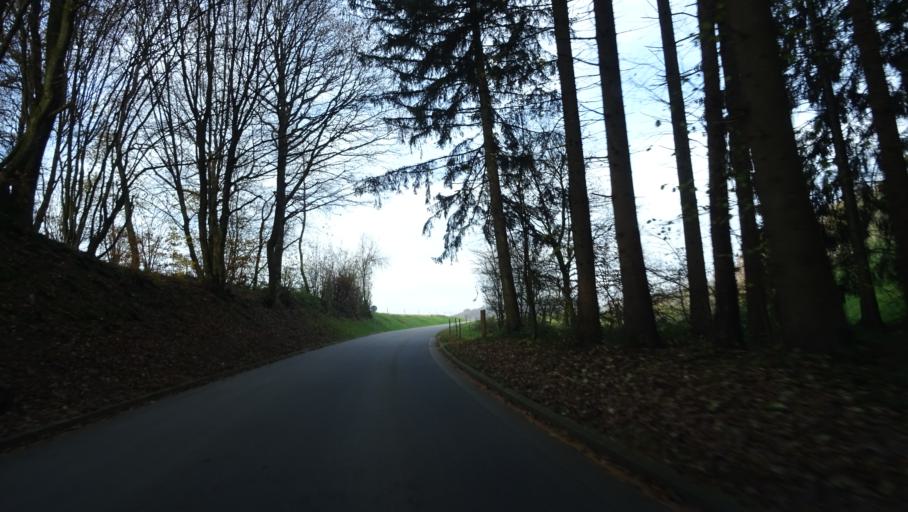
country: DE
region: Baden-Wuerttemberg
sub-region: Karlsruhe Region
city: Neckargerach
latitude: 49.4082
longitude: 9.0788
